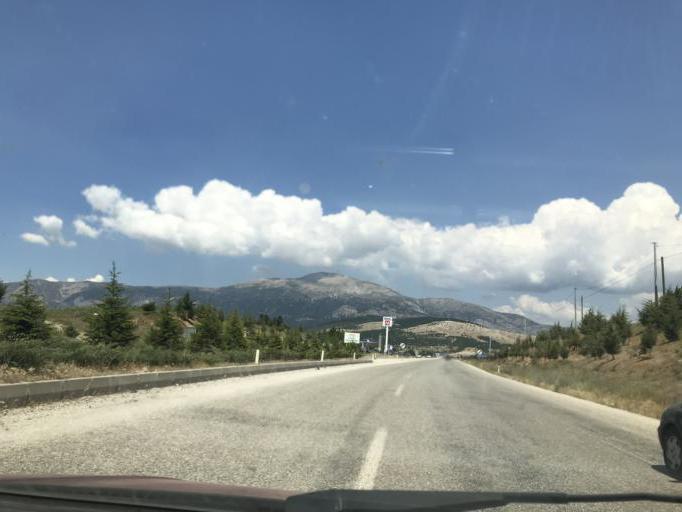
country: TR
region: Denizli
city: Serinhisar
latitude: 37.6208
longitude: 29.1943
